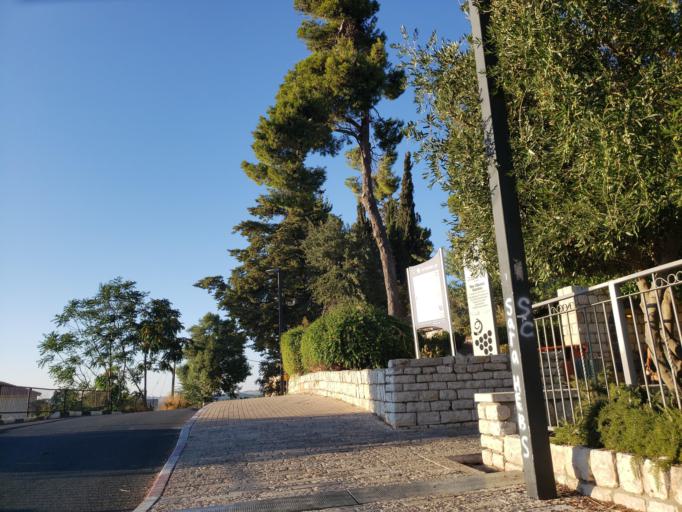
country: IL
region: Northern District
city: Safed
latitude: 32.9693
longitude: 35.4940
